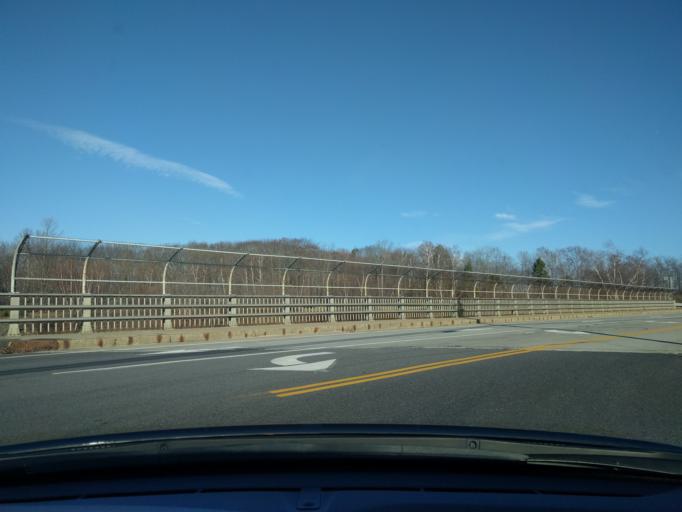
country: US
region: Maine
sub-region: Penobscot County
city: Brewer
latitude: 44.7803
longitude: -68.7593
